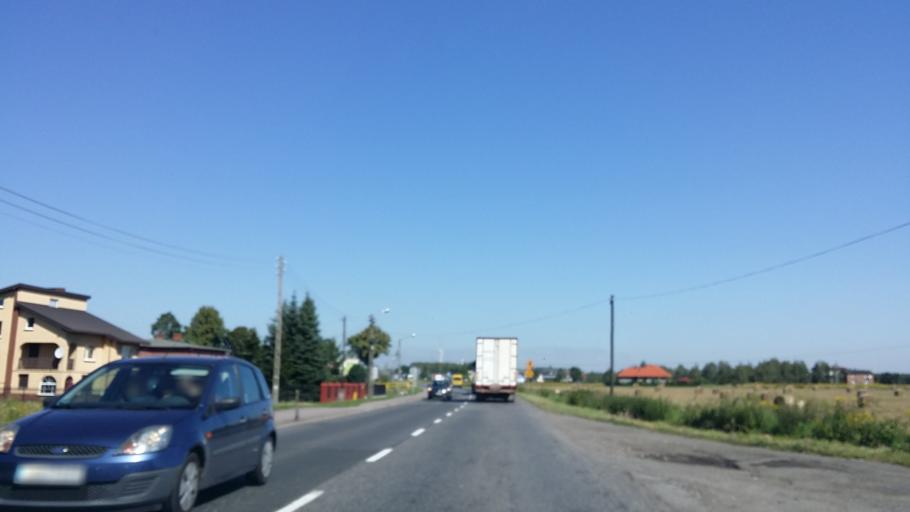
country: PL
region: Silesian Voivodeship
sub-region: Powiat bierunsko-ledzinski
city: Chelm Slaski
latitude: 50.1153
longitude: 19.2007
